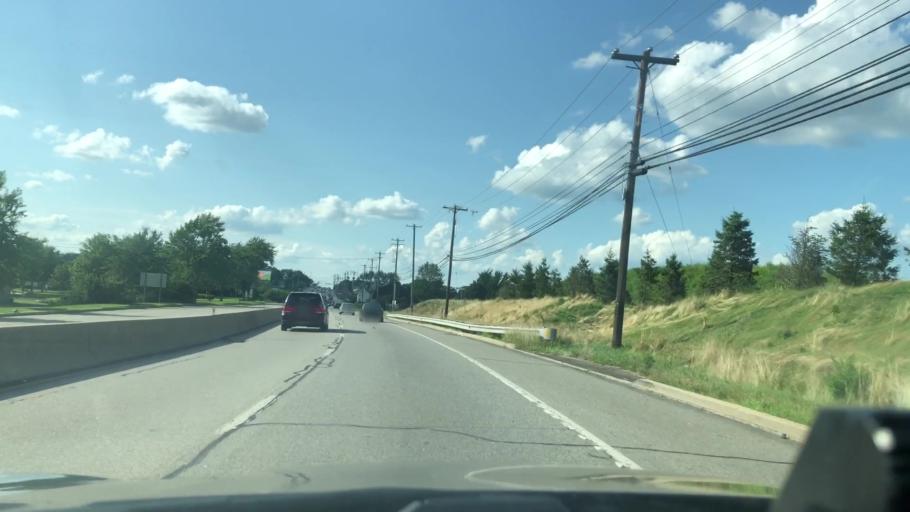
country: US
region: Pennsylvania
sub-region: Montgomery County
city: Spring House
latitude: 40.2114
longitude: -75.2251
